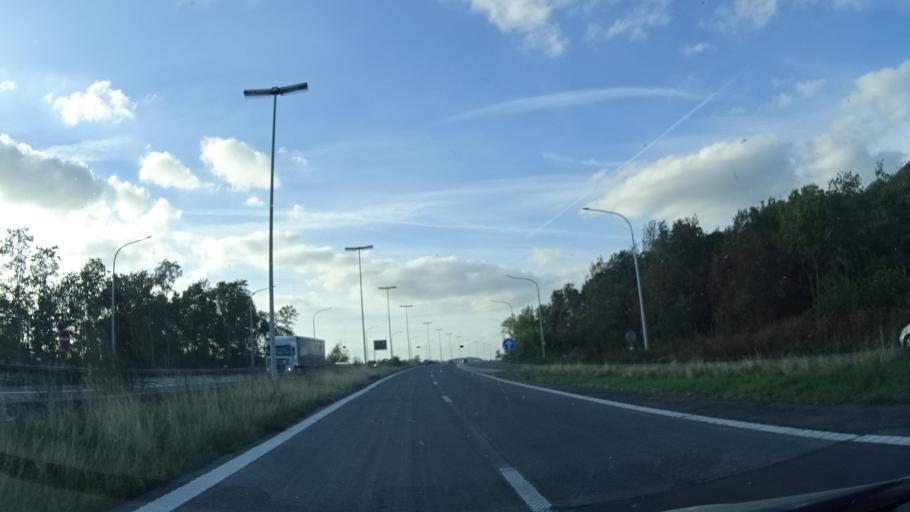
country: BE
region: Wallonia
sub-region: Province du Hainaut
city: Frameries
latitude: 50.4157
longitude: 3.9230
